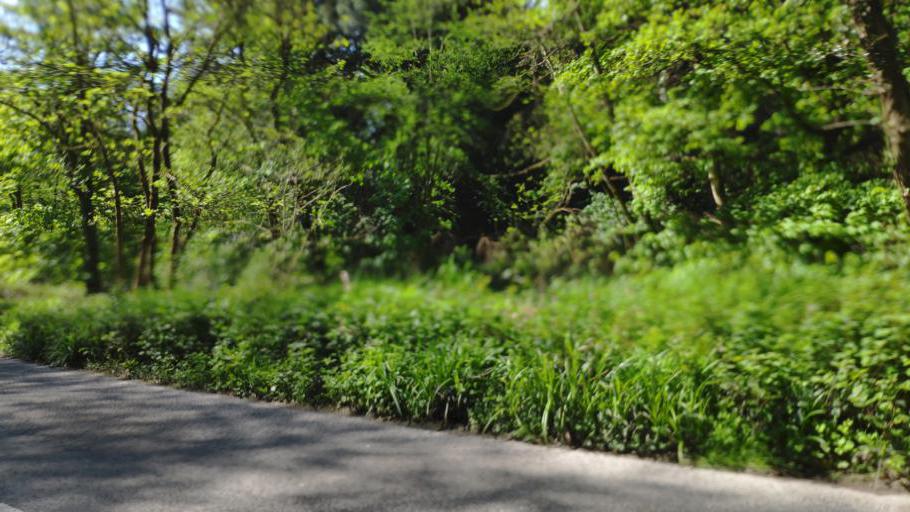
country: IE
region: Munster
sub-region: County Cork
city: Blarney
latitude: 51.9816
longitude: -8.5866
